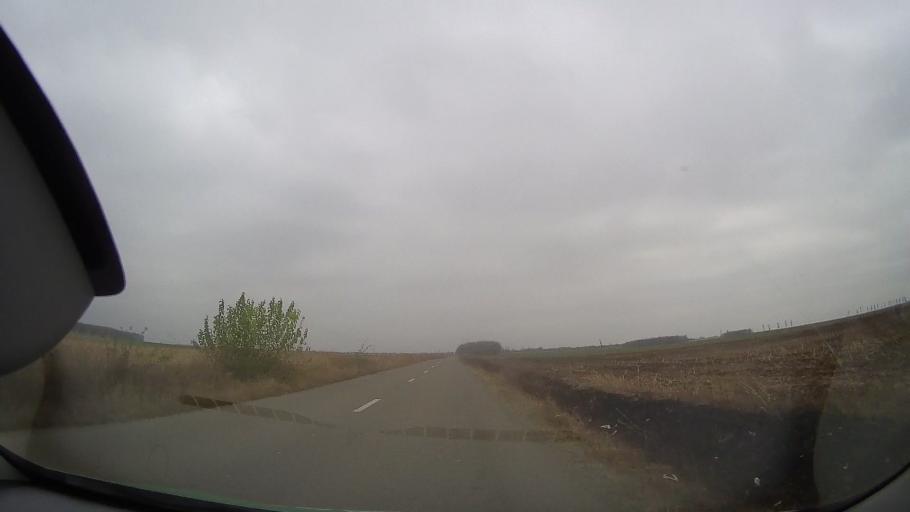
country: RO
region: Buzau
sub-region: Comuna Scutelnici
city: Scutelnici
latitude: 44.8660
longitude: 26.8940
